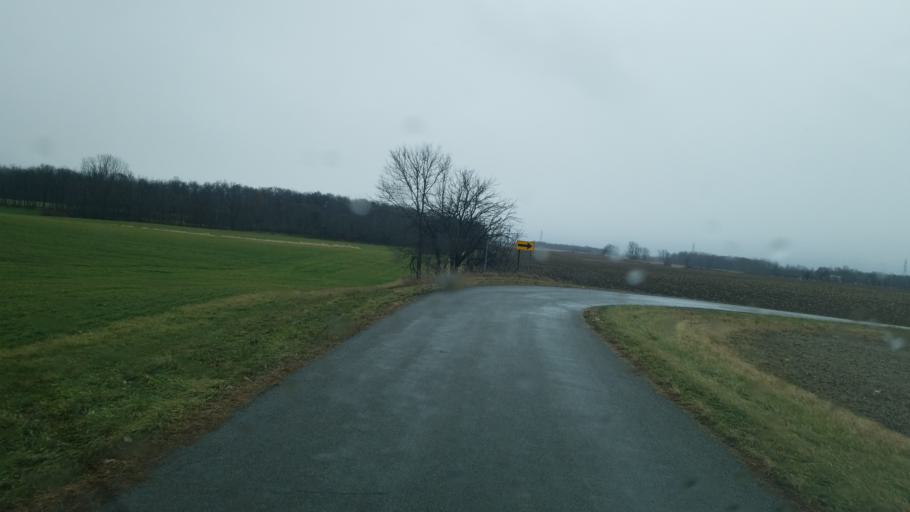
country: US
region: Ohio
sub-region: Hardin County
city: Kenton
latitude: 40.5509
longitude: -83.6537
